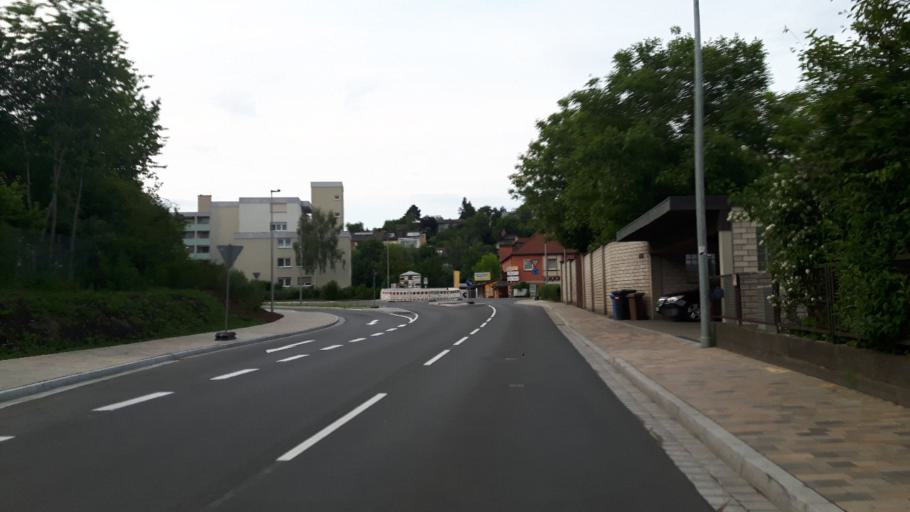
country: DE
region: Bavaria
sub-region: Regierungsbezirk Unterfranken
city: Wuerzburg
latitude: 49.8011
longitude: 9.9789
